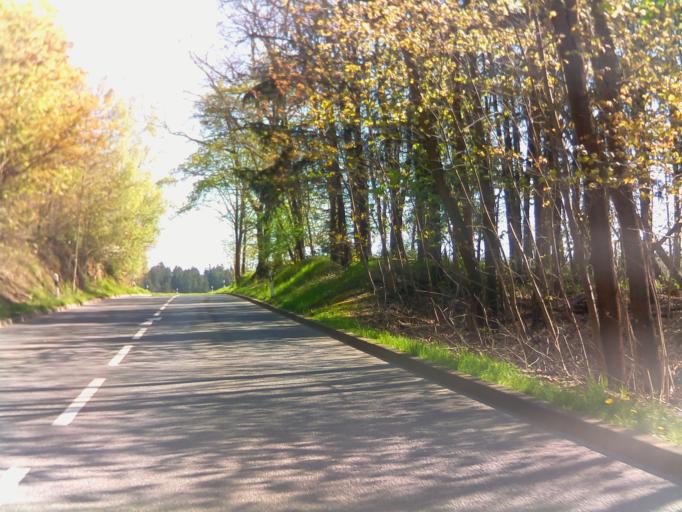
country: DE
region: Saxony
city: Neuensalz
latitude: 50.4989
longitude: 12.1836
